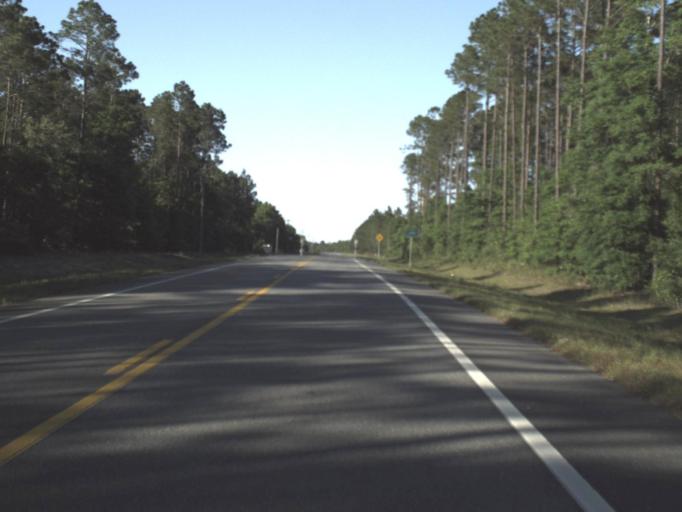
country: US
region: Florida
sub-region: Liberty County
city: Bristol
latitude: 30.4217
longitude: -84.7784
